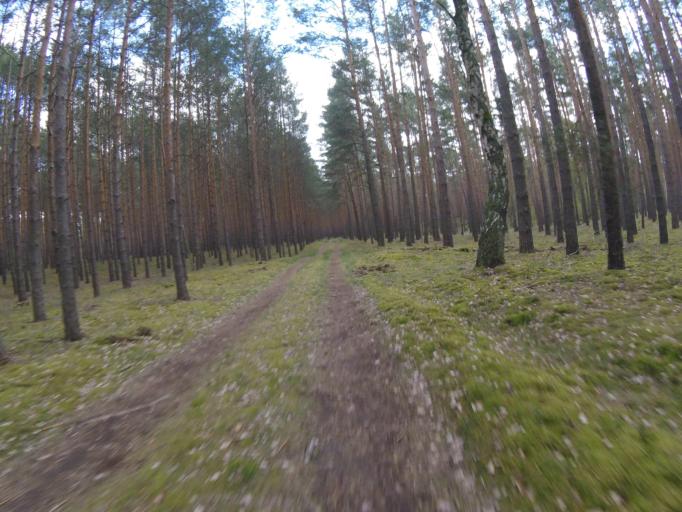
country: DE
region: Brandenburg
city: Bestensee
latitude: 52.2640
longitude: 13.6701
